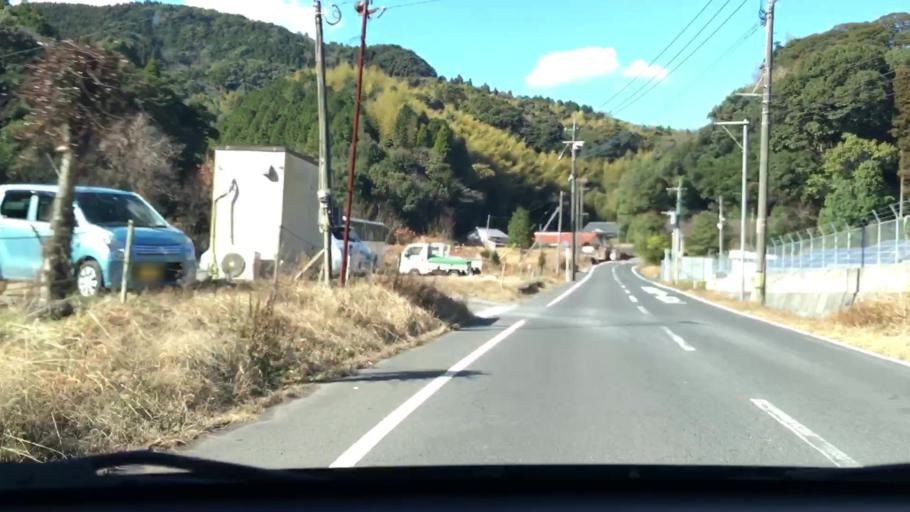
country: JP
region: Kagoshima
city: Ijuin
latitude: 31.7095
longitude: 130.4401
